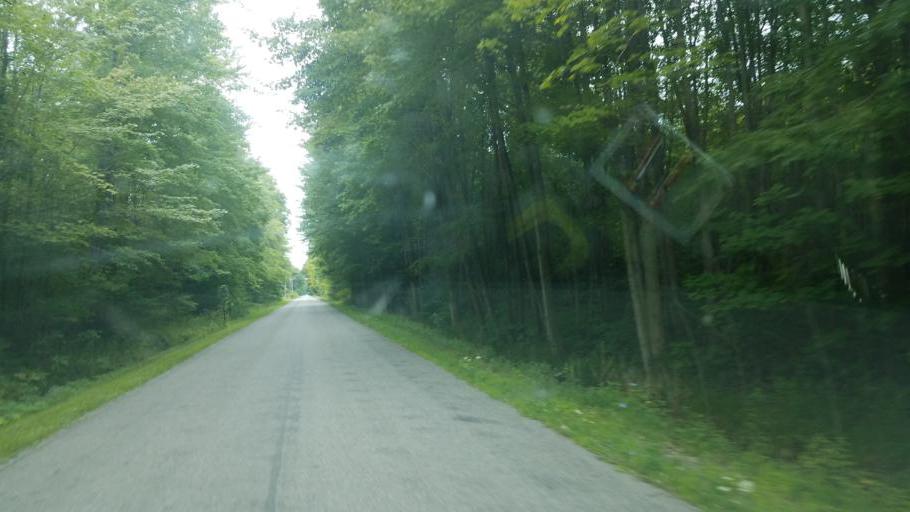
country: US
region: Pennsylvania
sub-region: Erie County
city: Lake City
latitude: 41.9938
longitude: -80.4408
